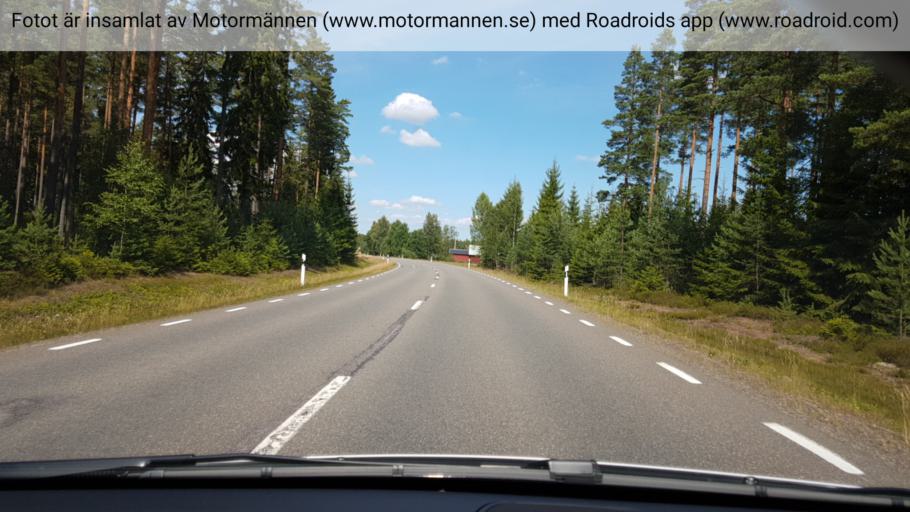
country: SE
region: Vaestra Goetaland
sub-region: Tibro Kommun
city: Tibro
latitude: 58.5071
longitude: 14.1640
